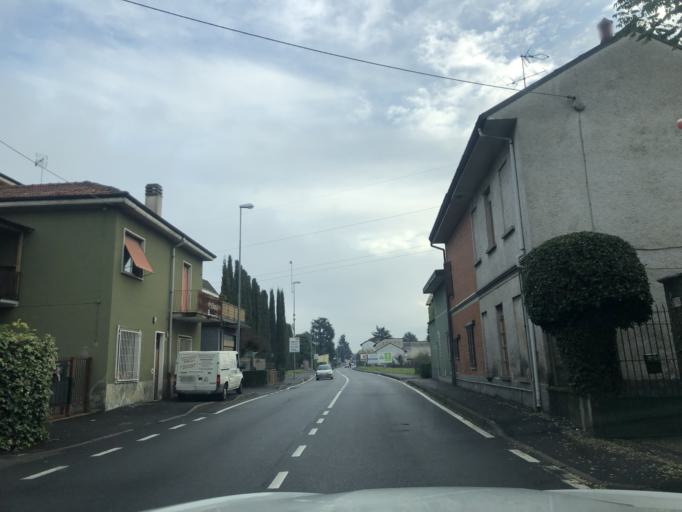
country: IT
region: Lombardy
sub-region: Citta metropolitana di Milano
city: Cologno Monzese
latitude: 45.5482
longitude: 9.2765
